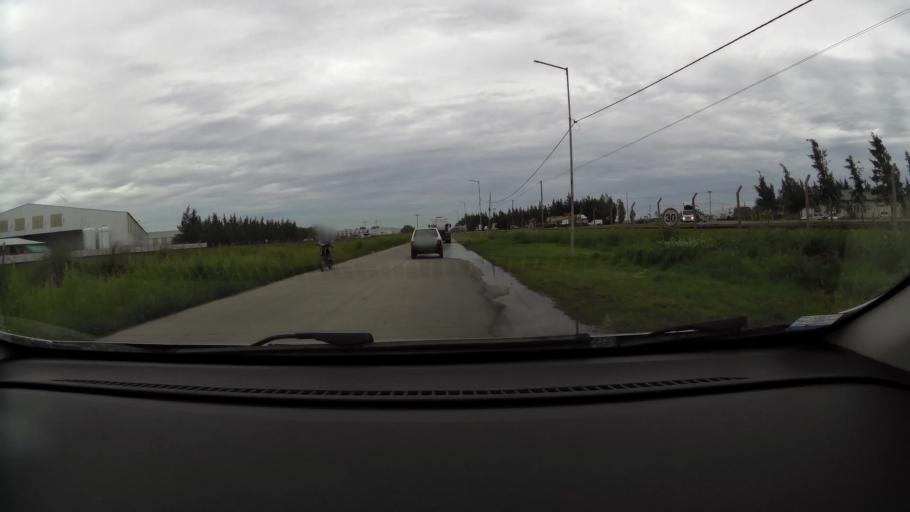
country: AR
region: Buenos Aires
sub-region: Partido de Zarate
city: Zarate
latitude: -34.0888
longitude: -59.0641
